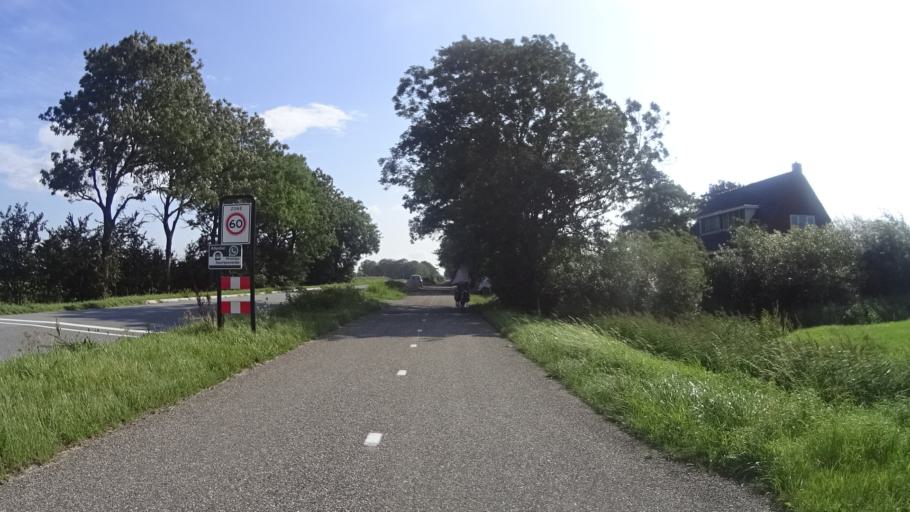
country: NL
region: Friesland
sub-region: Gemeente Franekeradeel
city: Tzum
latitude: 53.1931
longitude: 5.5973
